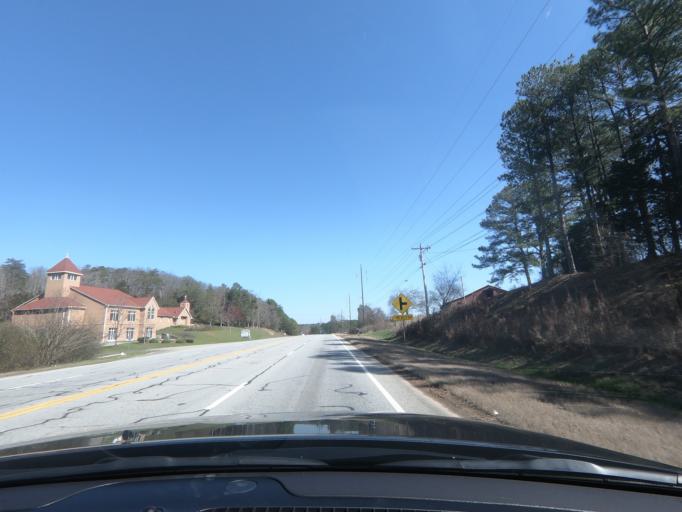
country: US
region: Georgia
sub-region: Gordon County
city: Calhoun
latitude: 34.4717
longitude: -84.9709
